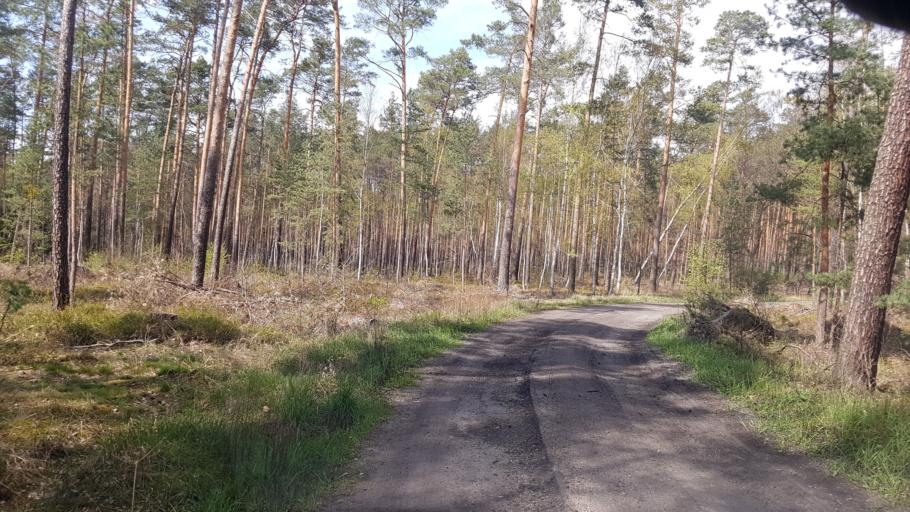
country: DE
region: Brandenburg
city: Plessa
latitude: 51.5451
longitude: 13.6578
